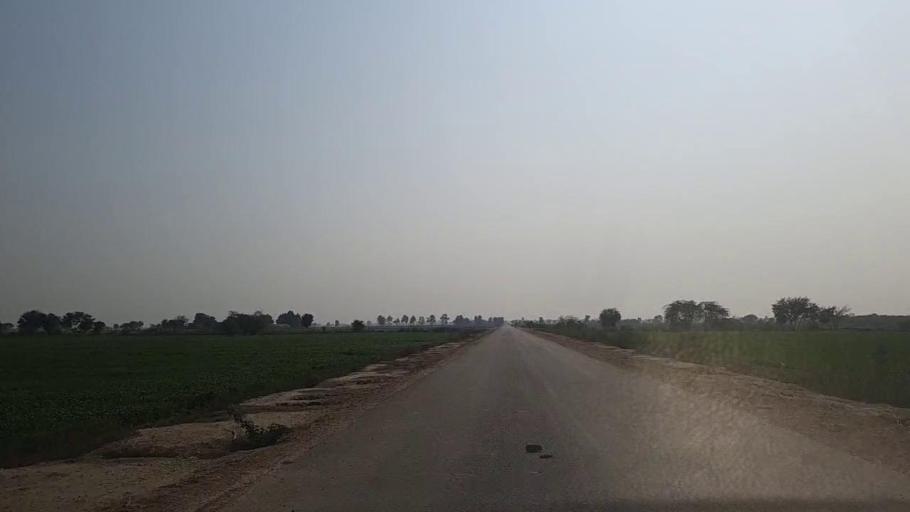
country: PK
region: Sindh
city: Jam Sahib
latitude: 26.3580
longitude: 68.5346
